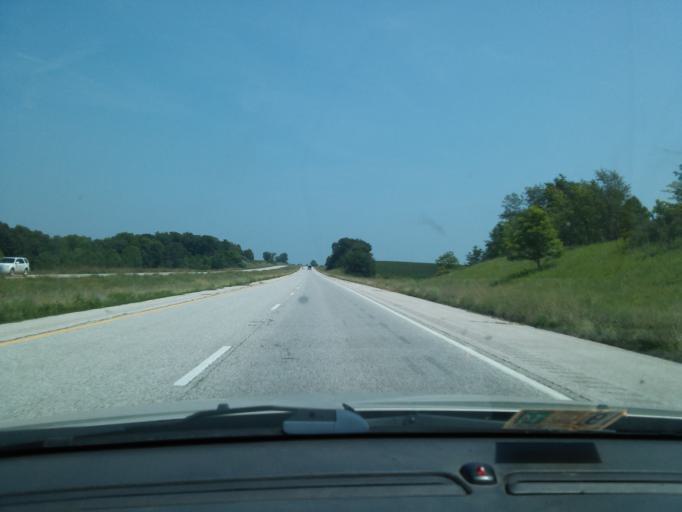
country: US
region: Illinois
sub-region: Pike County
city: Griggsville
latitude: 39.6752
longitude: -90.7381
